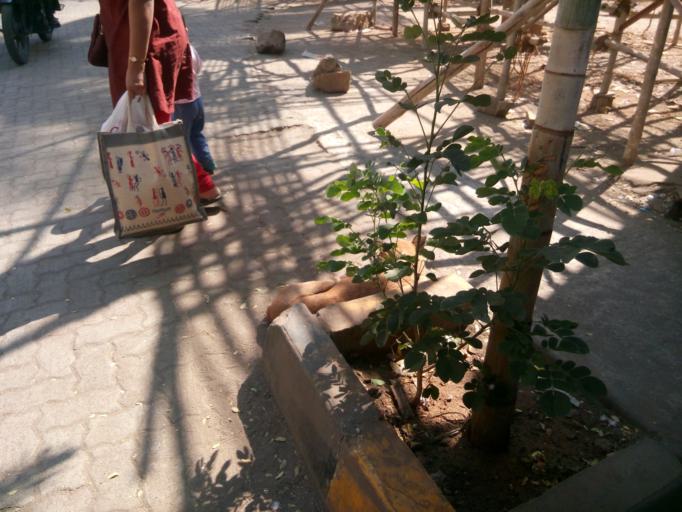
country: IN
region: Maharashtra
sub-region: Thane
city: Dombivli
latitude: 19.2075
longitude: 73.0948
